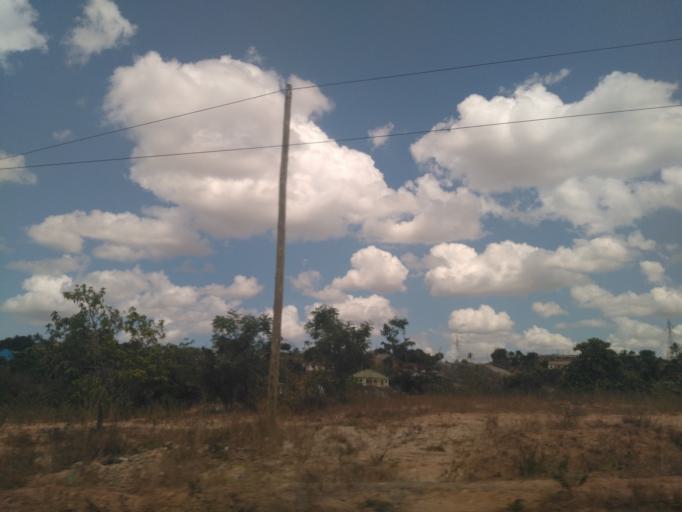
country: TZ
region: Dar es Salaam
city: Dar es Salaam
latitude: -6.9058
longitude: 39.2376
